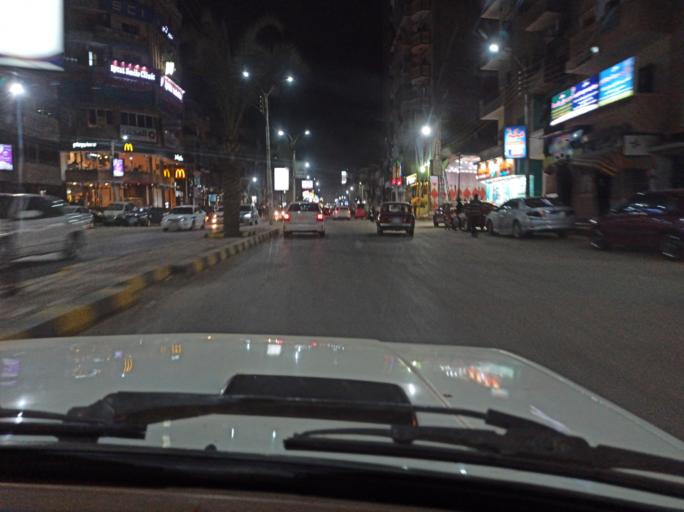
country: EG
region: Muhafazat Bani Suwayf
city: Bani Suwayf
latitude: 29.0712
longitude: 31.1030
